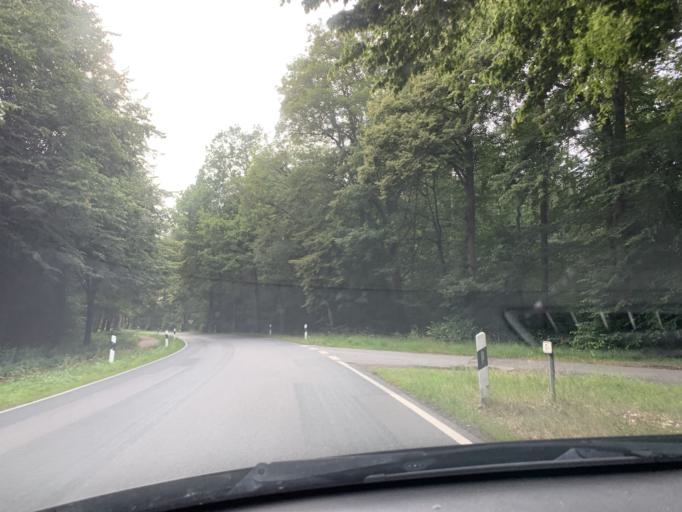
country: DE
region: Lower Saxony
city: Westerstede
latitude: 53.2750
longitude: 7.9383
